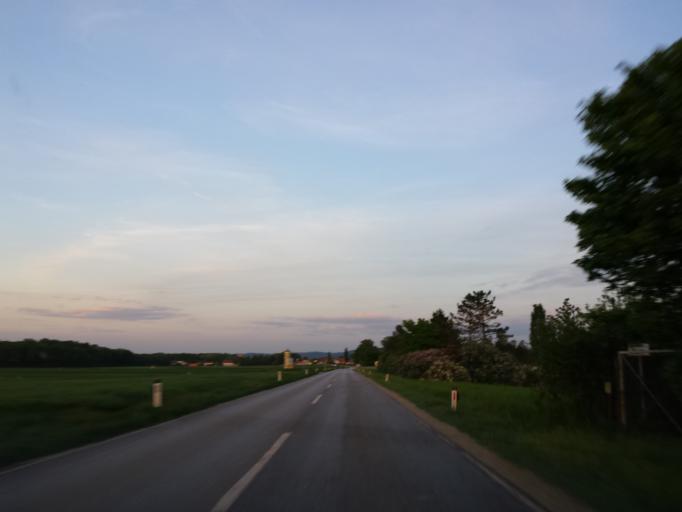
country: AT
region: Lower Austria
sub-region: Politischer Bezirk Tulln
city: Langenrohr
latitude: 48.3214
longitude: 15.9926
